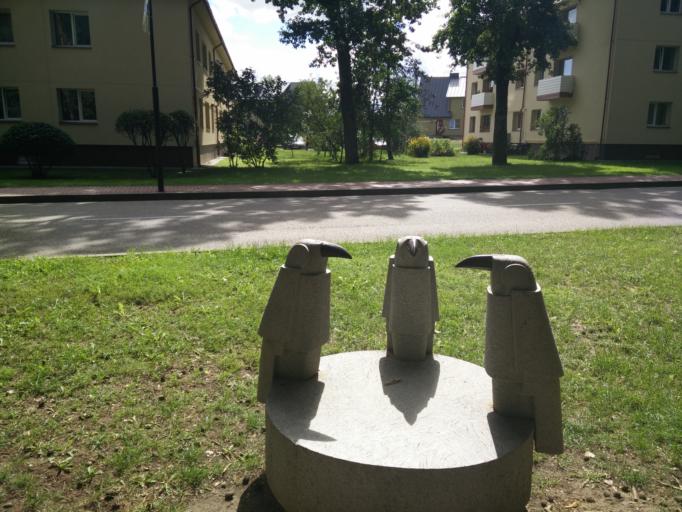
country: LT
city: Birstonas
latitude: 54.6074
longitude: 24.0320
